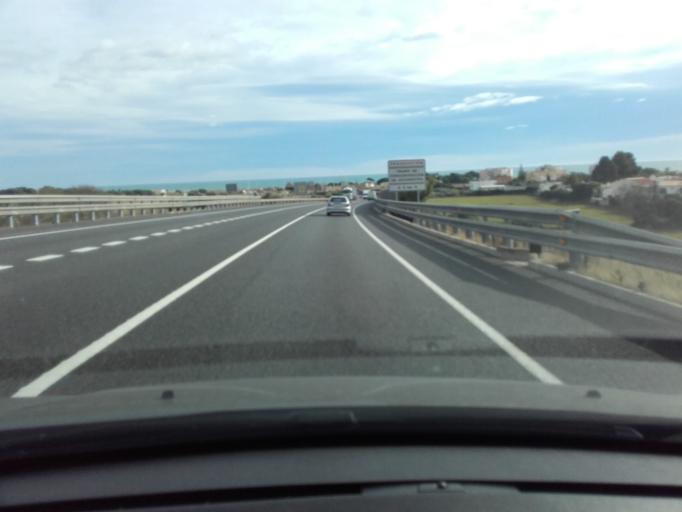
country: ES
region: Catalonia
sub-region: Provincia de Tarragona
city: Creixell
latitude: 41.1585
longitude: 1.4225
